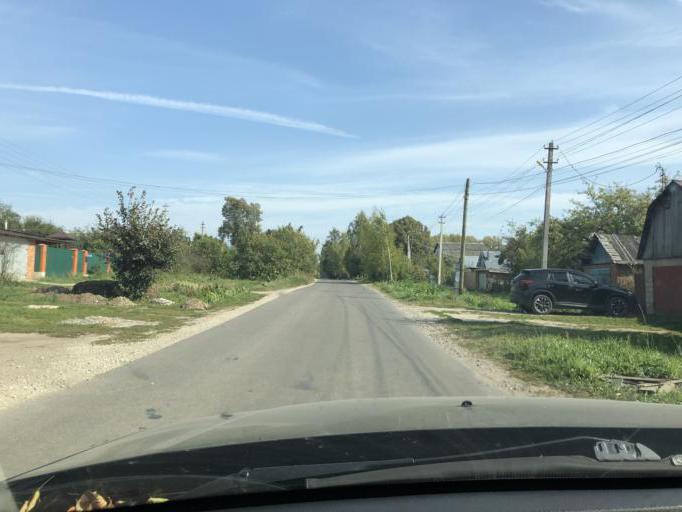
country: RU
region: Tula
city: Yasnogorsk
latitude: 54.4851
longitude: 37.6912
